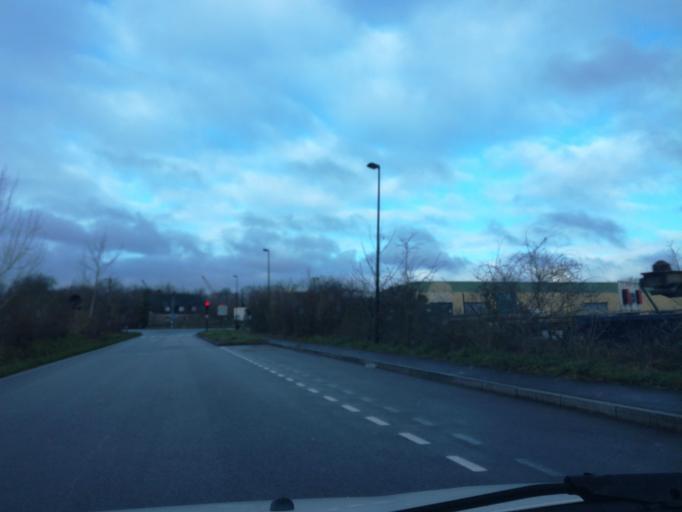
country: FR
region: Brittany
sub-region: Departement d'Ille-et-Vilaine
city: Saint-Jacques-de-la-Lande
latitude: 48.0770
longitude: -1.7410
